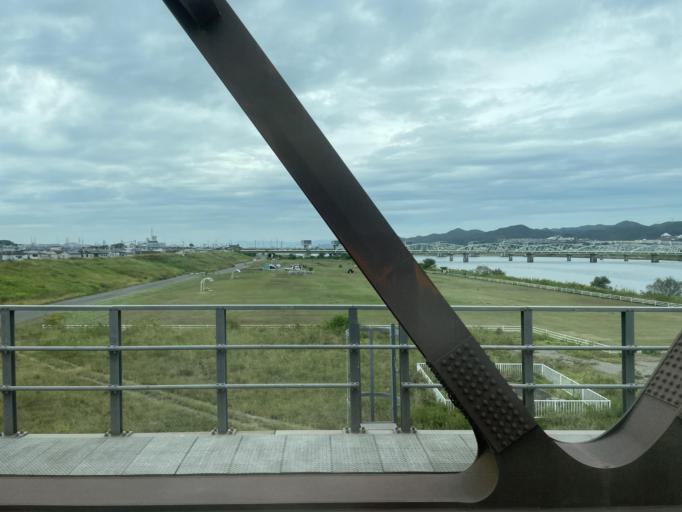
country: JP
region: Wakayama
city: Wakayama-shi
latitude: 34.2540
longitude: 135.2052
